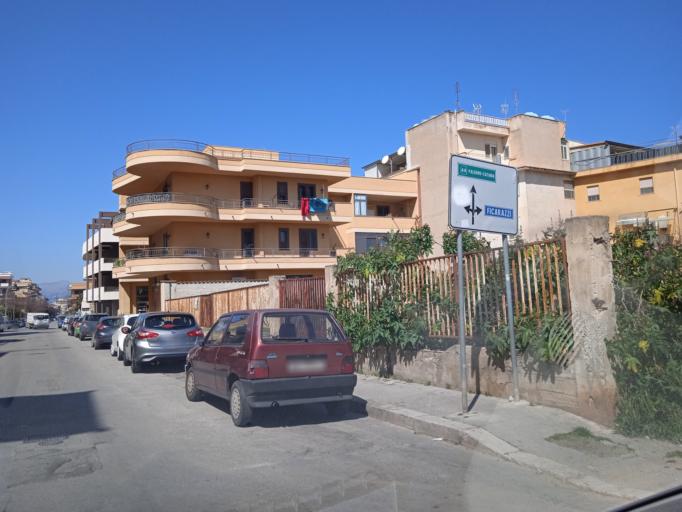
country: IT
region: Sicily
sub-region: Palermo
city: Villabate
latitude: 38.0775
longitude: 13.4485
